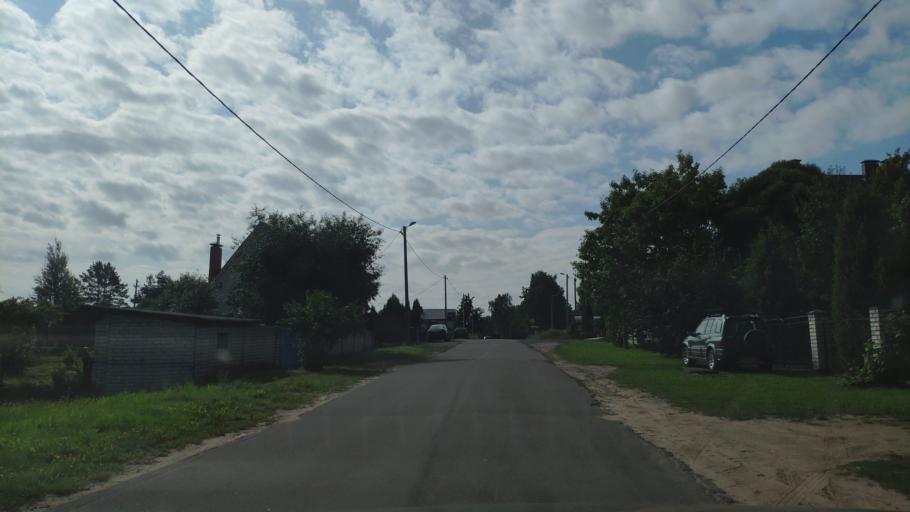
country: BY
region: Minsk
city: Zaslawye
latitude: 53.9943
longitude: 27.2832
